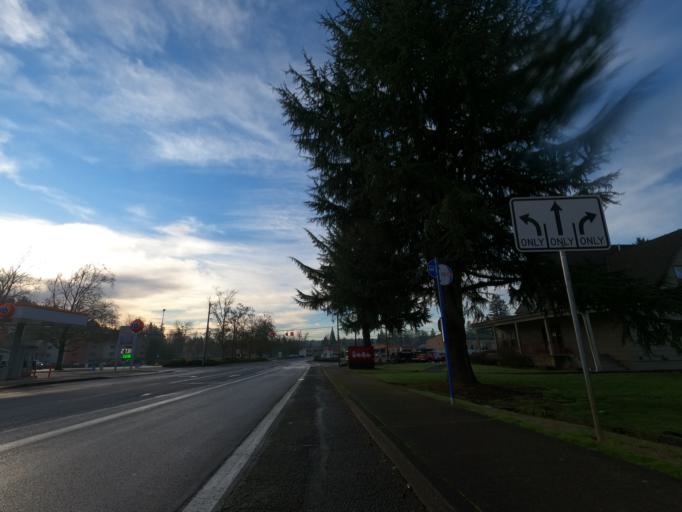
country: US
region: Oregon
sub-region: Clackamas County
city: Gladstone
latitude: 45.3822
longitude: -122.5834
